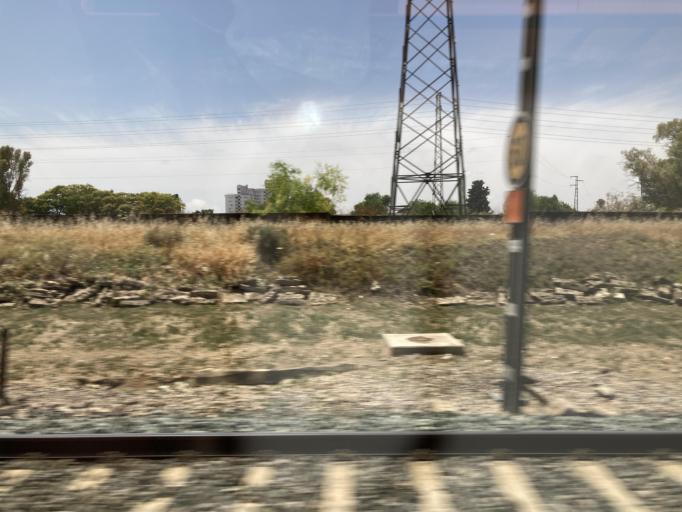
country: ES
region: Andalusia
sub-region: Provincia de Sevilla
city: Sevilla
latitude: 37.3508
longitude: -5.9710
